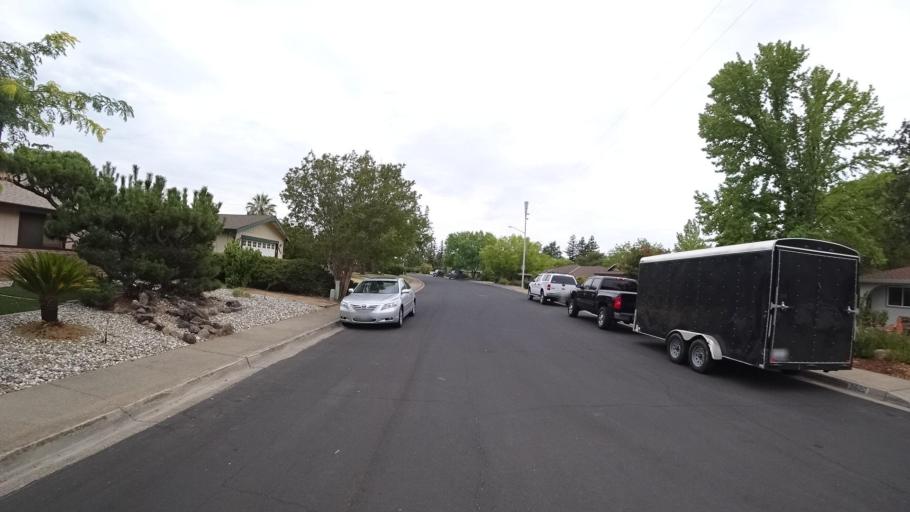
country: US
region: California
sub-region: Placer County
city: Rocklin
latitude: 38.7954
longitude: -121.2529
